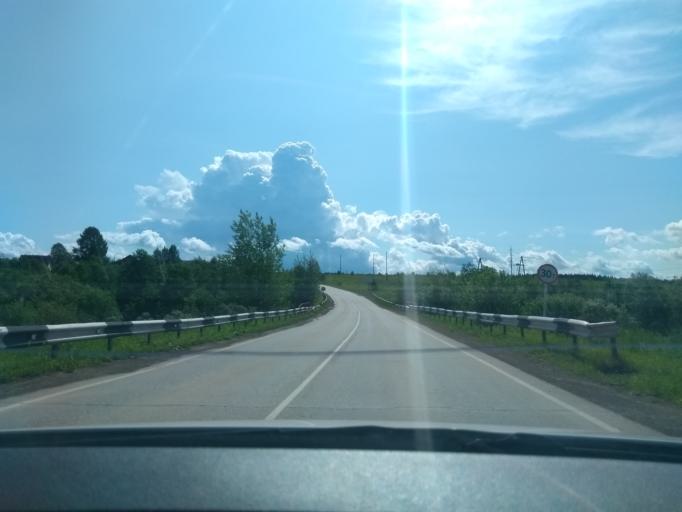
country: RU
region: Perm
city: Bershet'
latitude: 57.8118
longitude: 56.4564
